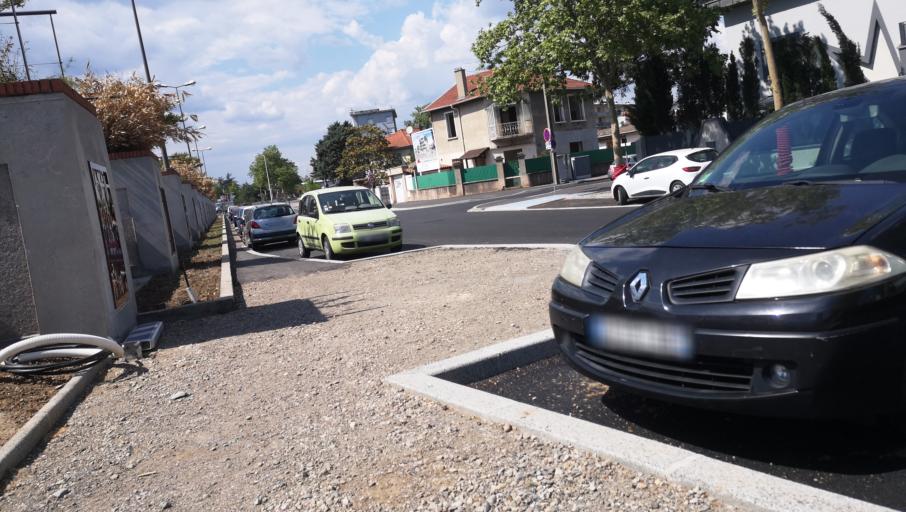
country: FR
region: Rhone-Alpes
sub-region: Departement du Rhone
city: Venissieux
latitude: 45.7187
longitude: 4.8900
